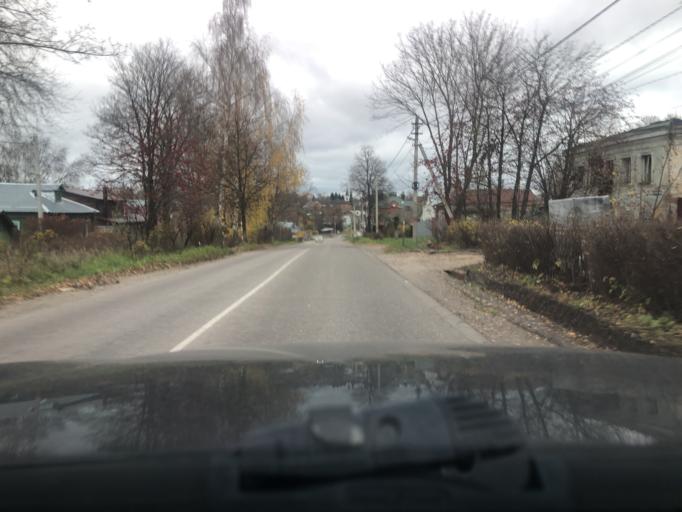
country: RU
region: Moskovskaya
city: Sergiyev Posad
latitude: 56.3009
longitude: 38.1239
